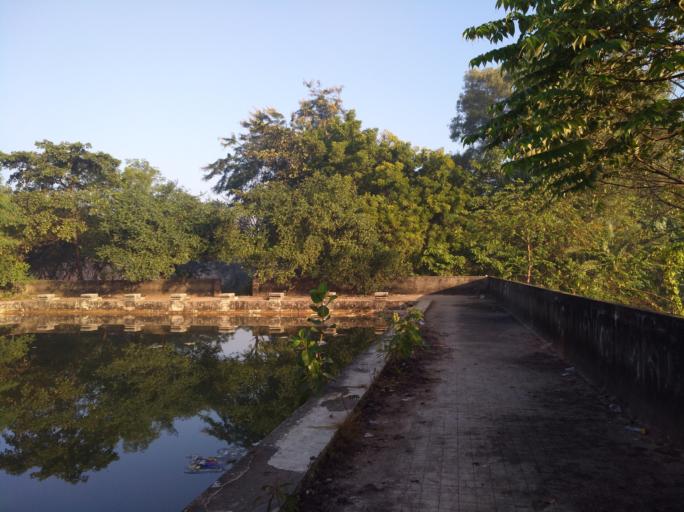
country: BD
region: Dhaka
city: Tungi
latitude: 23.8741
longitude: 90.2657
